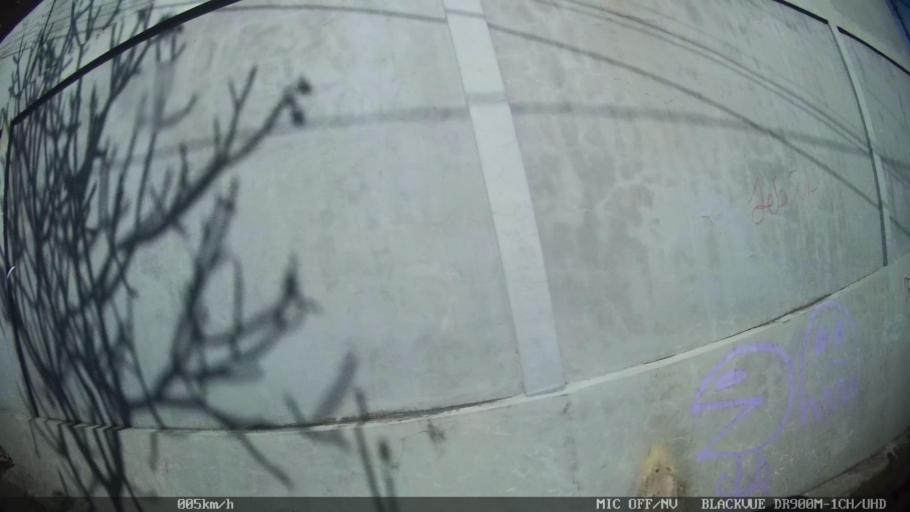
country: ID
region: Bali
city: Denpasar
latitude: -8.6536
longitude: 115.1746
